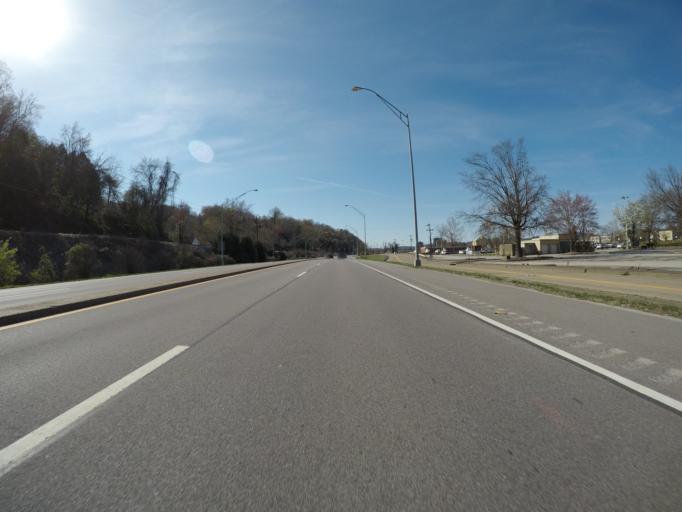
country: US
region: West Virginia
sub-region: Kanawha County
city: Charleston
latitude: 38.3371
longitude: -81.6275
